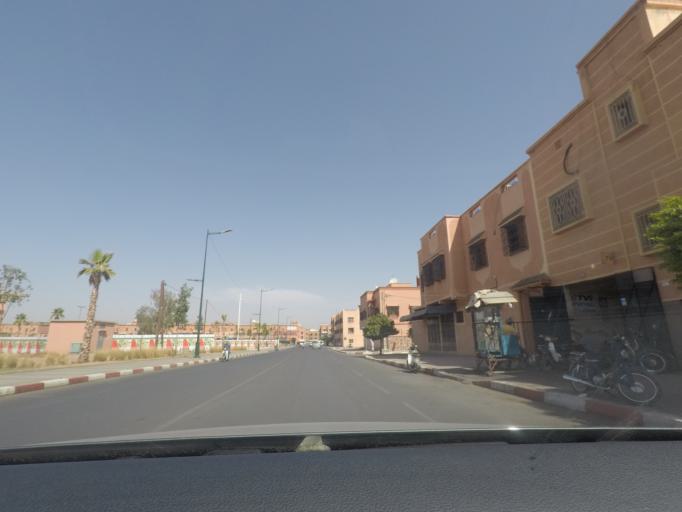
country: MA
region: Marrakech-Tensift-Al Haouz
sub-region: Marrakech
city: Marrakesh
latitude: 31.5927
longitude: -8.0281
